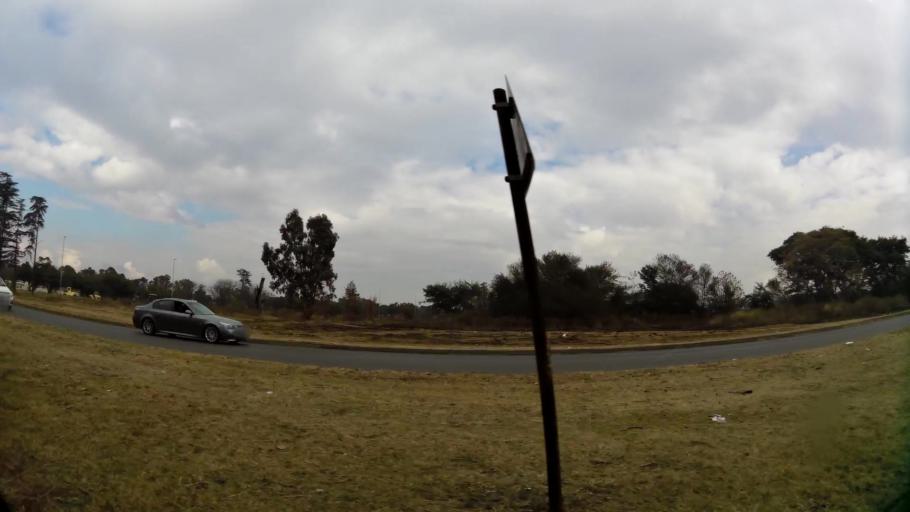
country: ZA
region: Gauteng
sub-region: Sedibeng District Municipality
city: Vanderbijlpark
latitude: -26.7068
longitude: 27.8599
